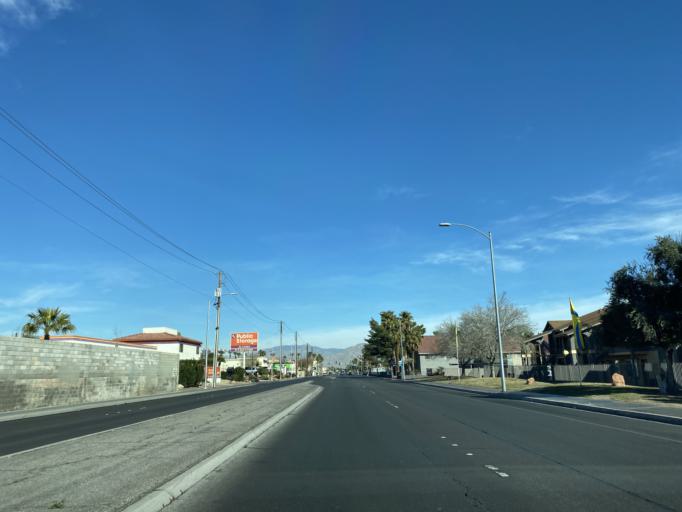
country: US
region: Nevada
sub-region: Clark County
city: Spring Valley
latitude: 36.1932
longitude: -115.2239
